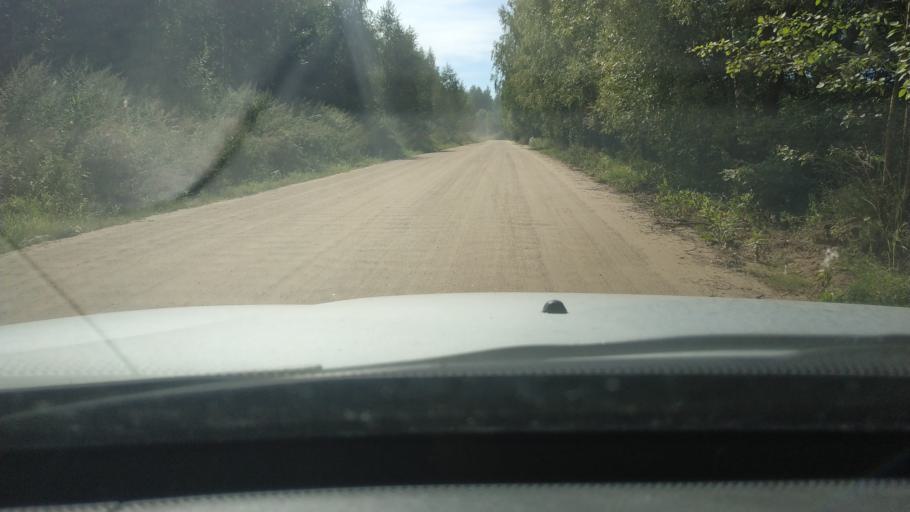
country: RU
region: Kostroma
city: Kosmynino
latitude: 57.7725
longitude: 40.7303
